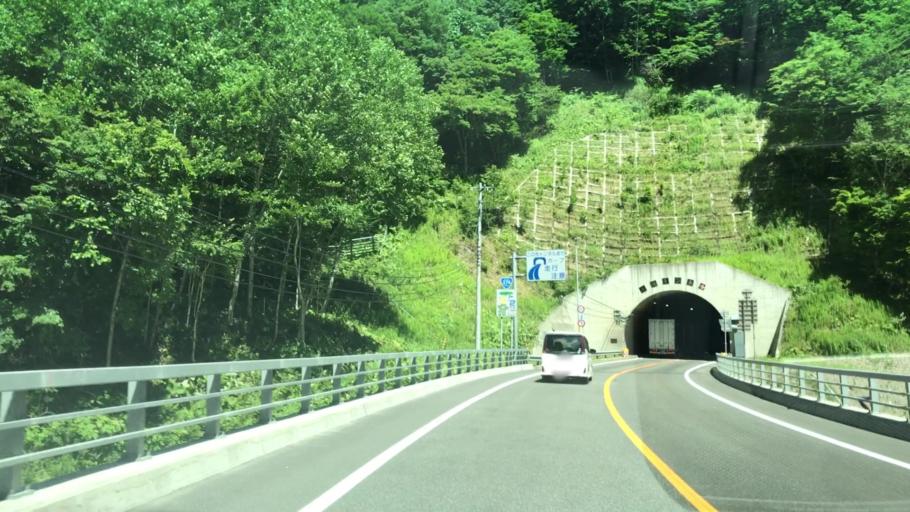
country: JP
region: Hokkaido
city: Shimo-furano
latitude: 42.9457
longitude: 142.5978
